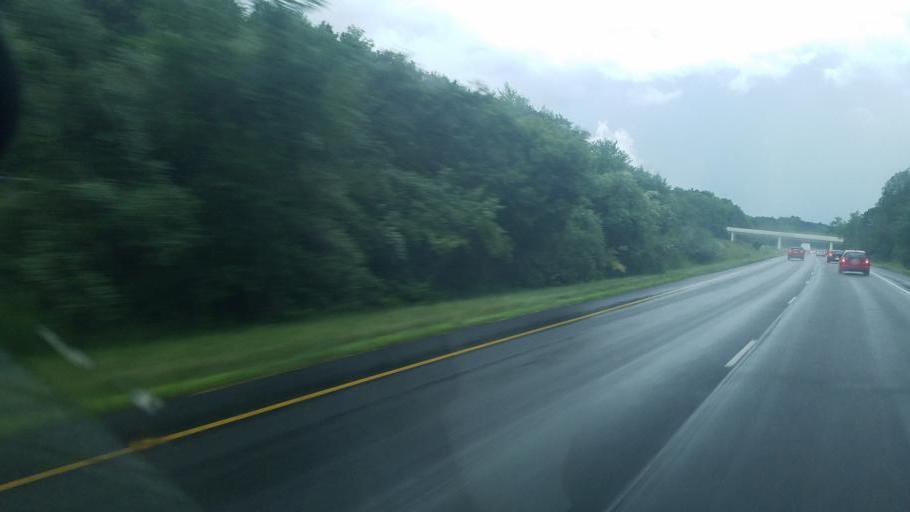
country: US
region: Ohio
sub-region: Summit County
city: Norton
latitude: 41.0725
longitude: -81.6656
